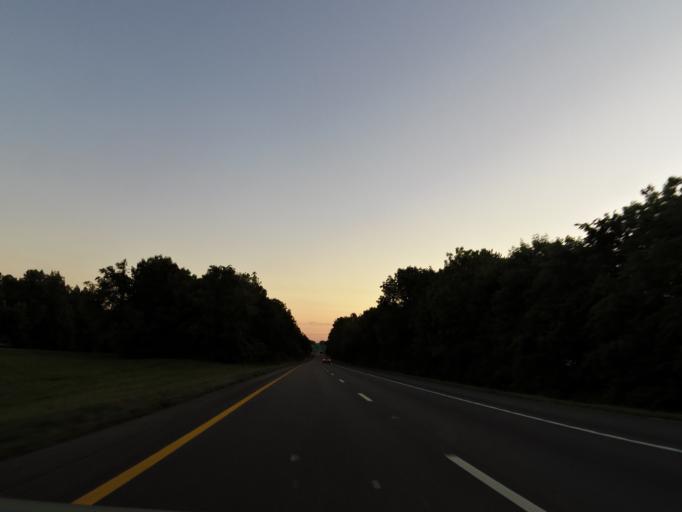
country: US
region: Tennessee
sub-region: Jefferson County
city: White Pine
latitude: 36.0844
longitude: -83.3629
